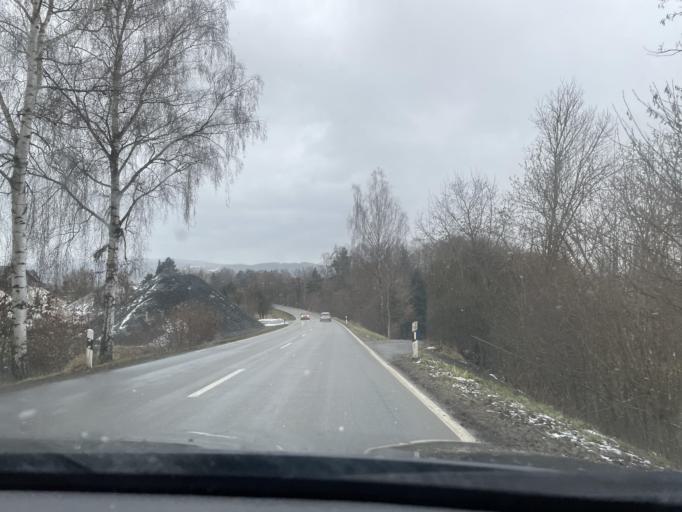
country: DE
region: Bavaria
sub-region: Upper Palatinate
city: Kotzting
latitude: 49.1951
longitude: 12.8549
